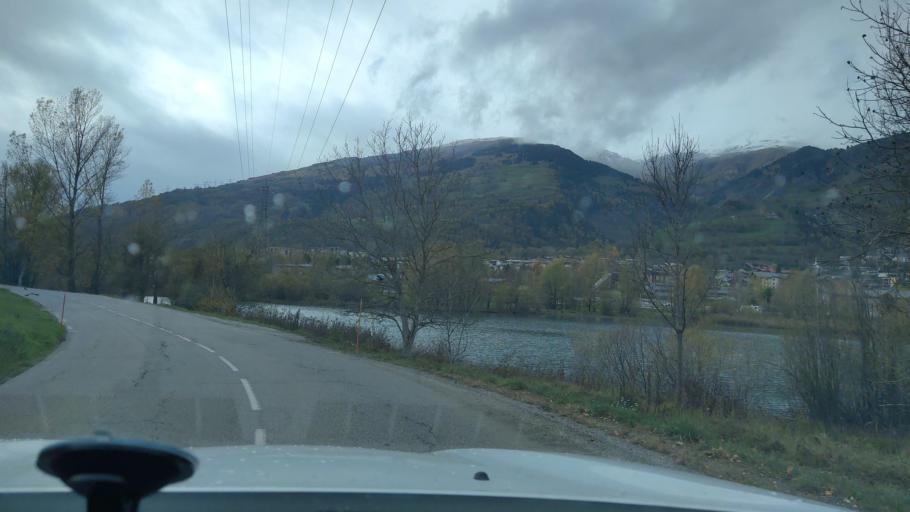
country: FR
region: Rhone-Alpes
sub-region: Departement de la Savoie
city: Bourg-Saint-Maurice
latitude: 45.6143
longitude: 6.7783
